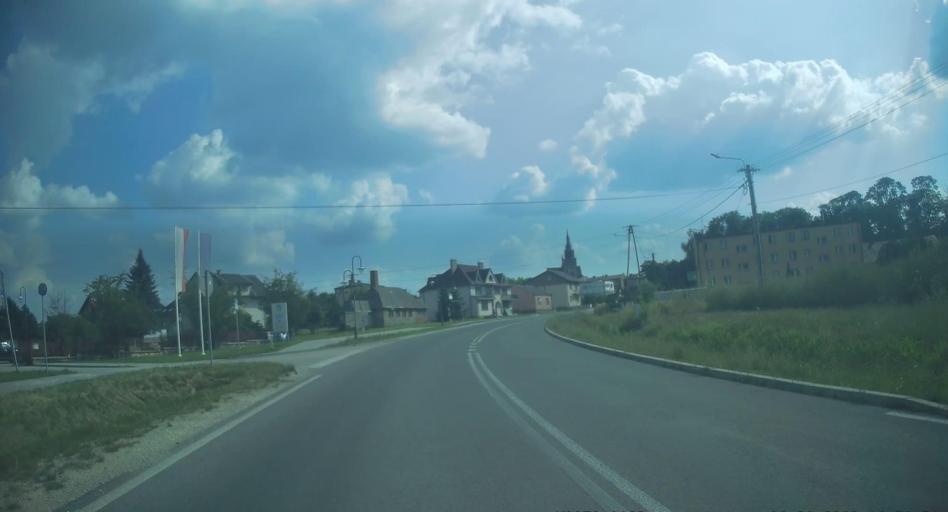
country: PL
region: Swietokrzyskie
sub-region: Powiat kielecki
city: Lopuszno
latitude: 50.9521
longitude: 20.2520
